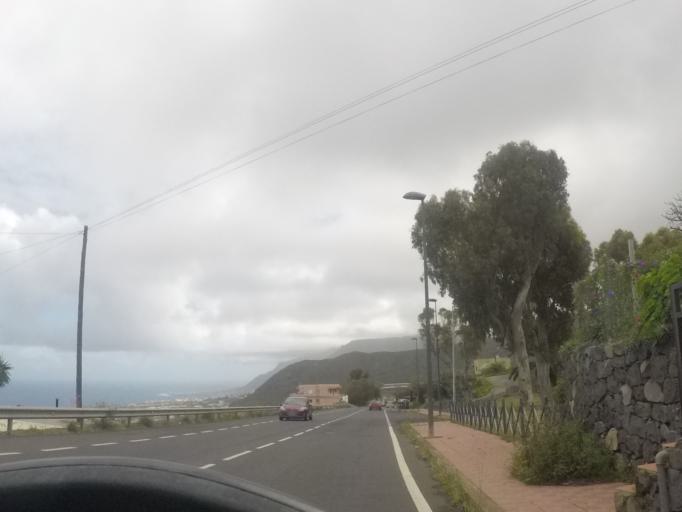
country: ES
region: Canary Islands
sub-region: Provincia de Santa Cruz de Tenerife
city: Tacoronte
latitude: 28.5126
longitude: -16.3934
